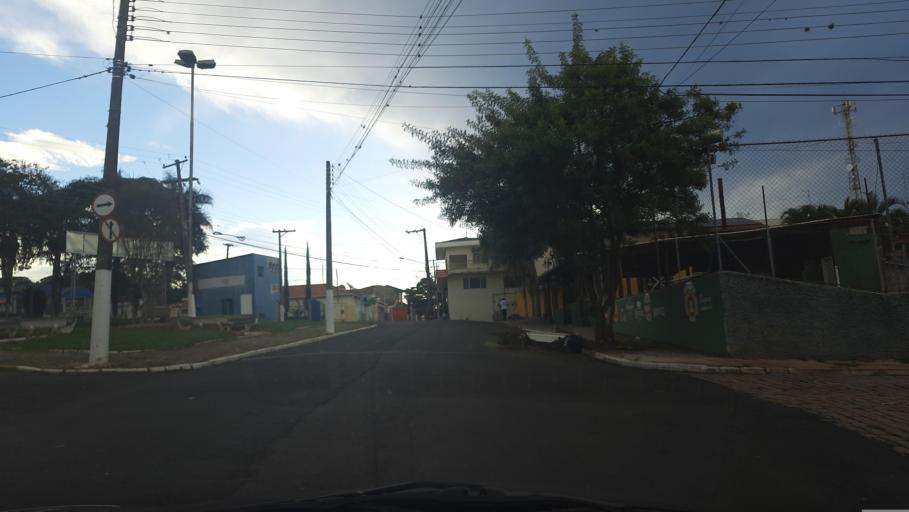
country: BR
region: Sao Paulo
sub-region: Casa Branca
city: Casa Branca
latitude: -21.7746
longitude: -47.0799
